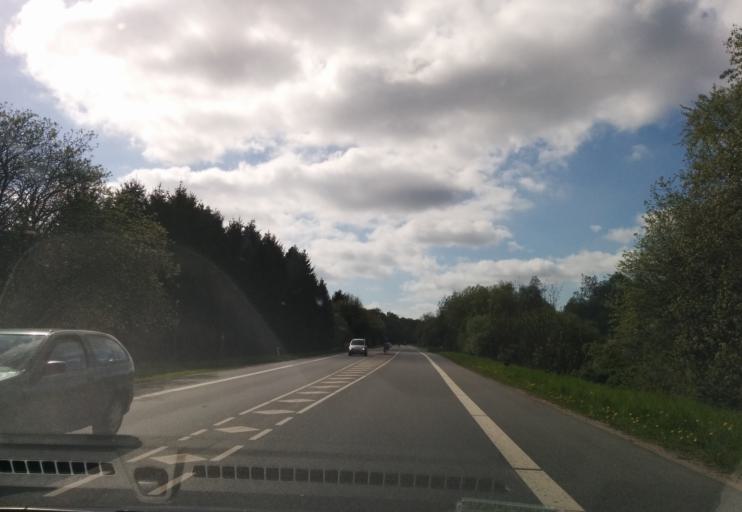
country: DK
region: South Denmark
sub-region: Assens Kommune
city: Vissenbjerg
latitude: 55.3918
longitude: 10.1189
